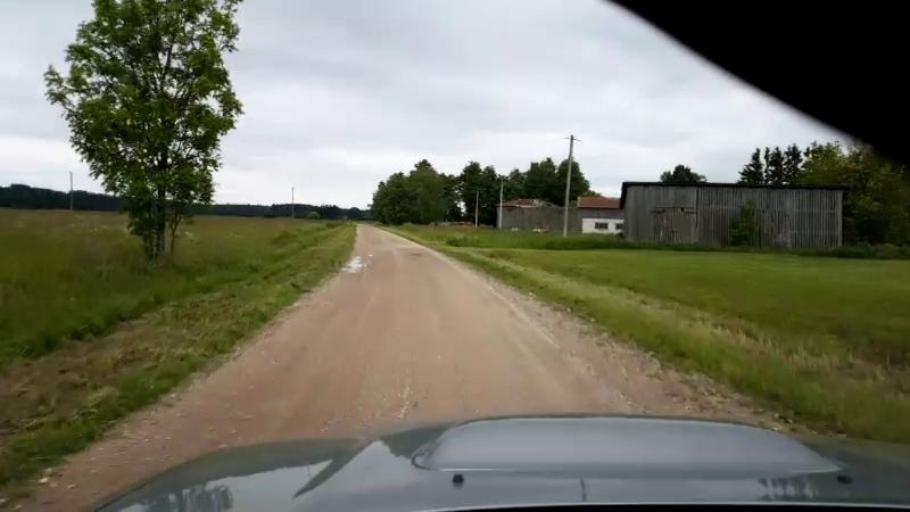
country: EE
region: Paernumaa
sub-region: Halinga vald
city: Parnu-Jaagupi
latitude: 58.5371
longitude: 24.5597
